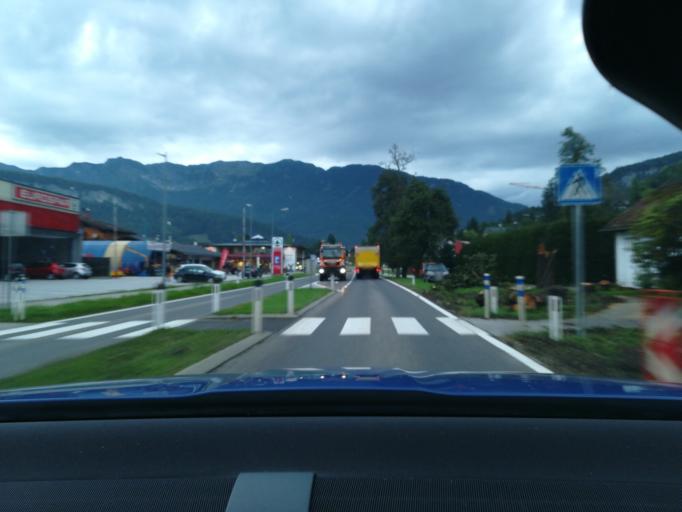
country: AT
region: Upper Austria
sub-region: Politischer Bezirk Gmunden
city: Bad Goisern
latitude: 47.6459
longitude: 13.6159
